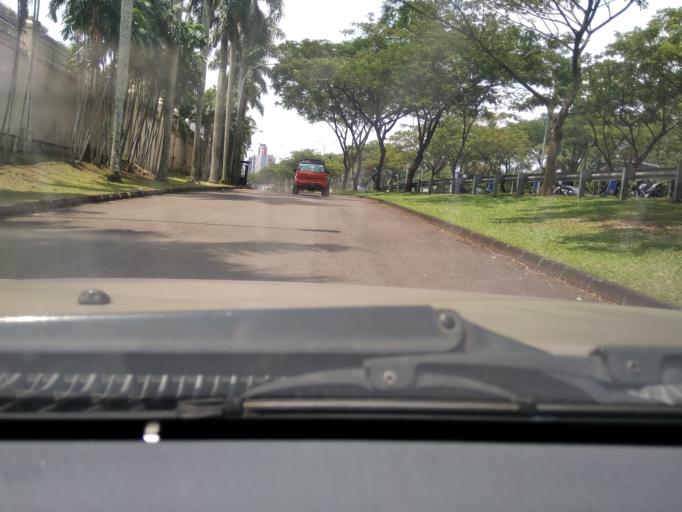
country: ID
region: West Java
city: Serpong
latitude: -6.2810
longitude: 106.6584
